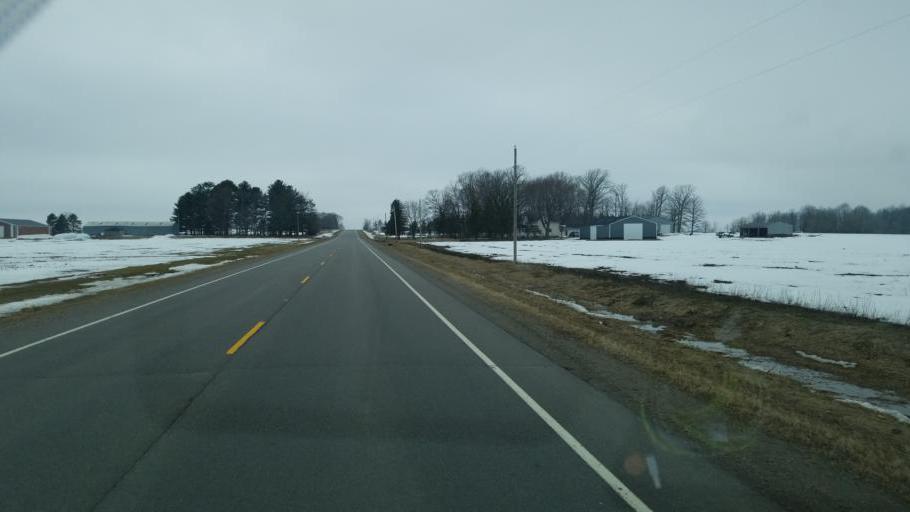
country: US
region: Wisconsin
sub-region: Marathon County
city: Spencer
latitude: 44.6561
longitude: -90.3224
